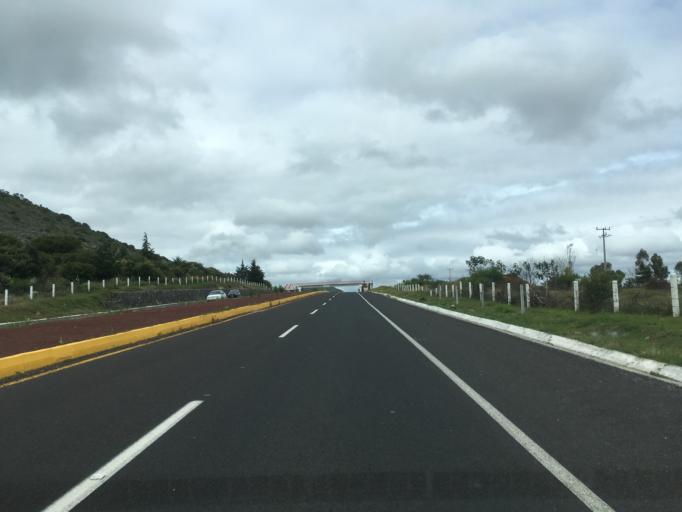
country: MX
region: Hidalgo
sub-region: Atotonilco el Grande
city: La Estancia
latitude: 20.3324
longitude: -98.7024
